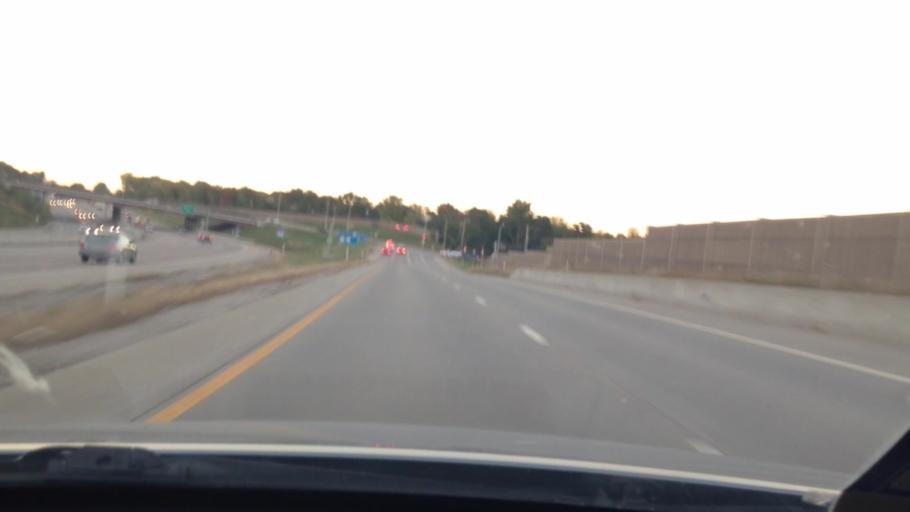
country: US
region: Kansas
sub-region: Johnson County
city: Lenexa
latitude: 38.9540
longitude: -94.7057
